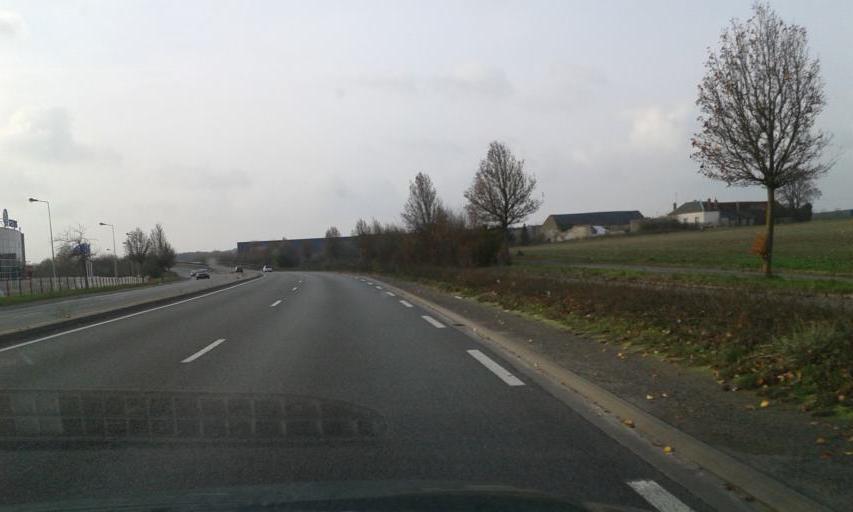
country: FR
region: Centre
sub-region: Departement du Loiret
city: Saran
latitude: 47.9531
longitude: 1.8553
